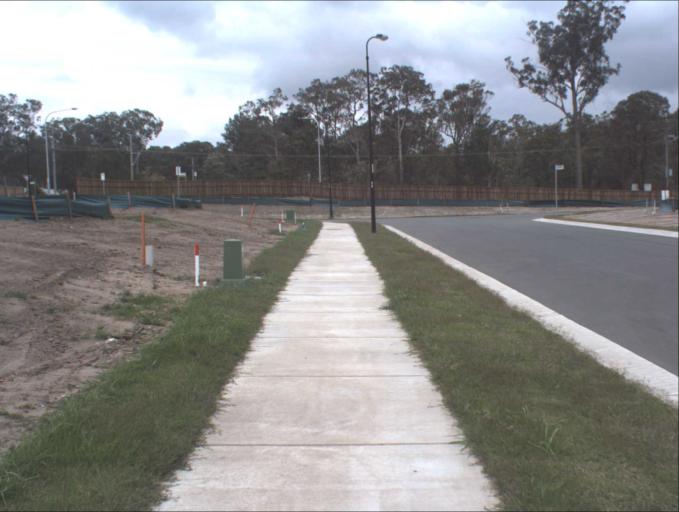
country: AU
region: Queensland
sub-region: Logan
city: Logan Reserve
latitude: -27.7119
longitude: 153.1075
